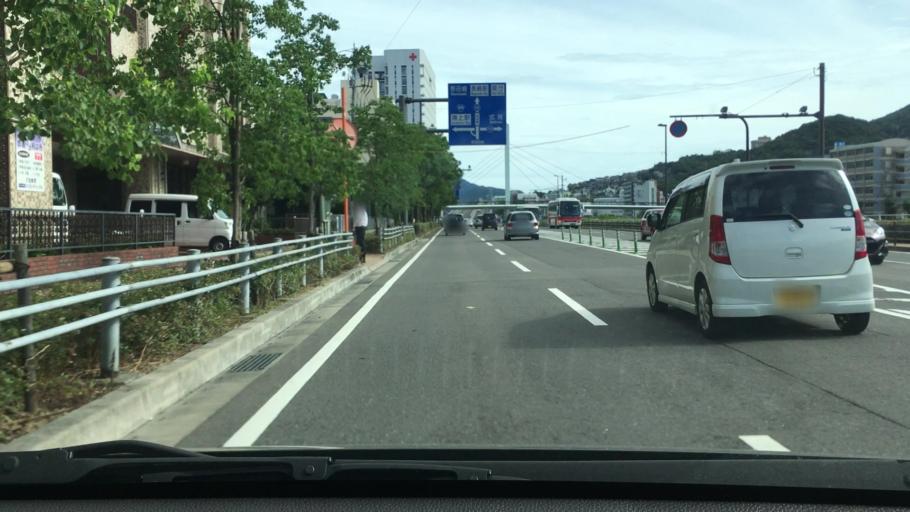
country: JP
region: Nagasaki
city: Nagasaki-shi
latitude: 32.7682
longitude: 129.8624
